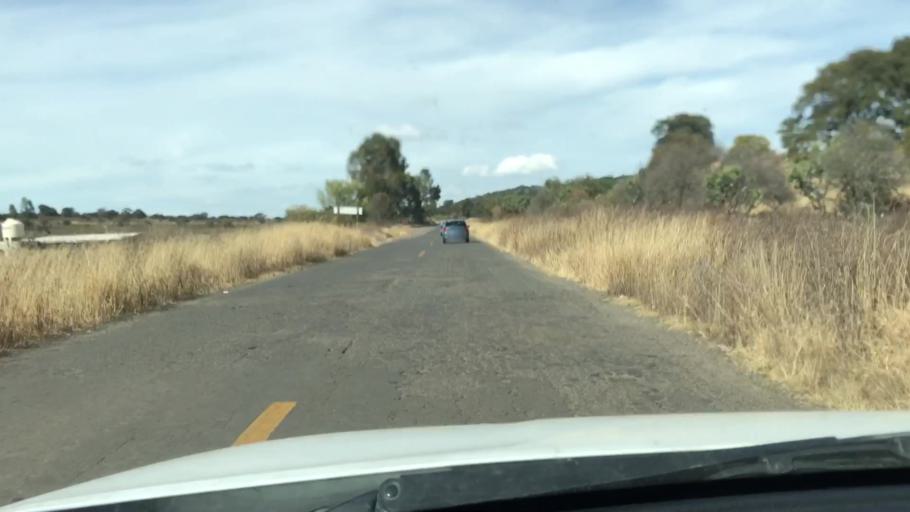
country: MX
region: Jalisco
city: Chiquilistlan
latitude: 20.1846
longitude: -103.7242
